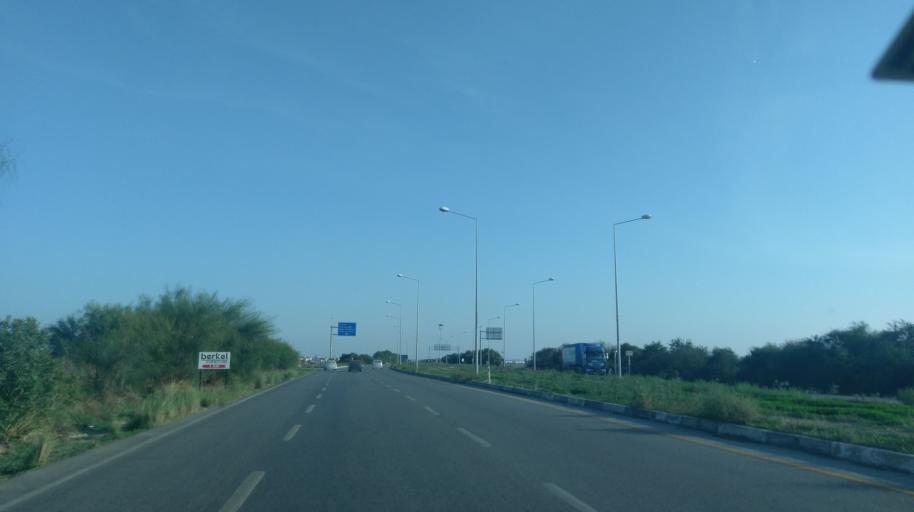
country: CY
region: Ammochostos
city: Acheritou
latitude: 35.1542
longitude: 33.8447
